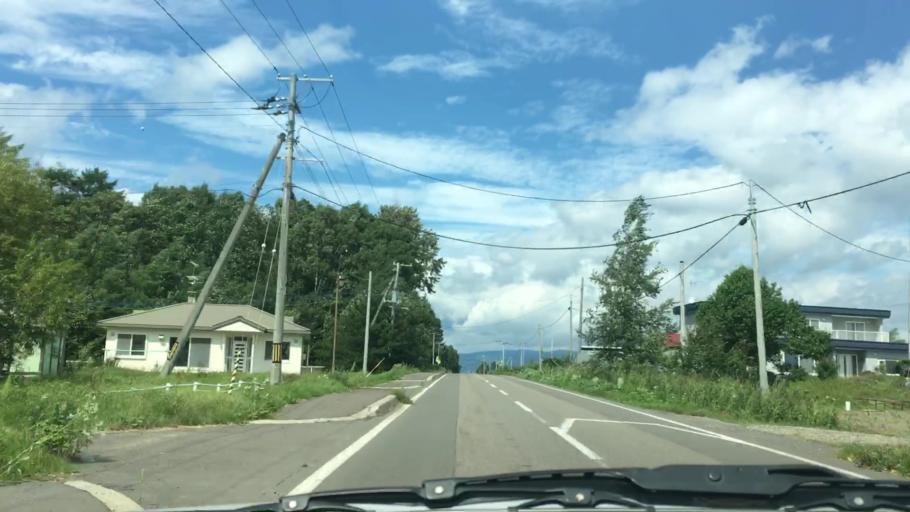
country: JP
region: Hokkaido
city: Otofuke
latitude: 43.2674
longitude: 143.3861
